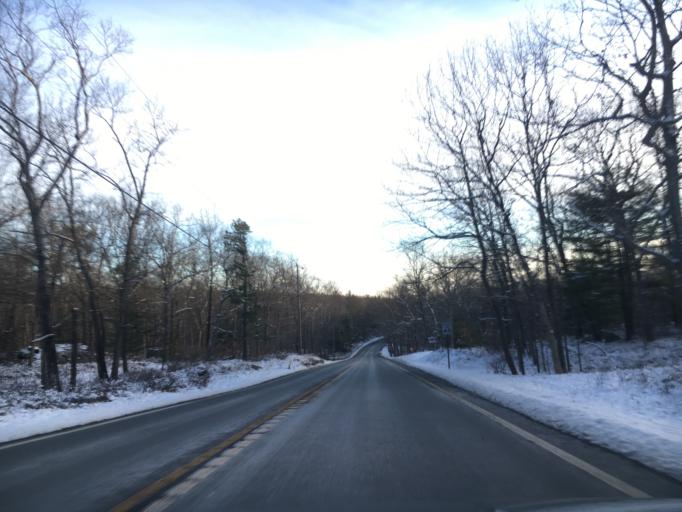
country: US
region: Pennsylvania
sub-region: Pike County
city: Hemlock Farms
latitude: 41.3164
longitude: -75.1107
